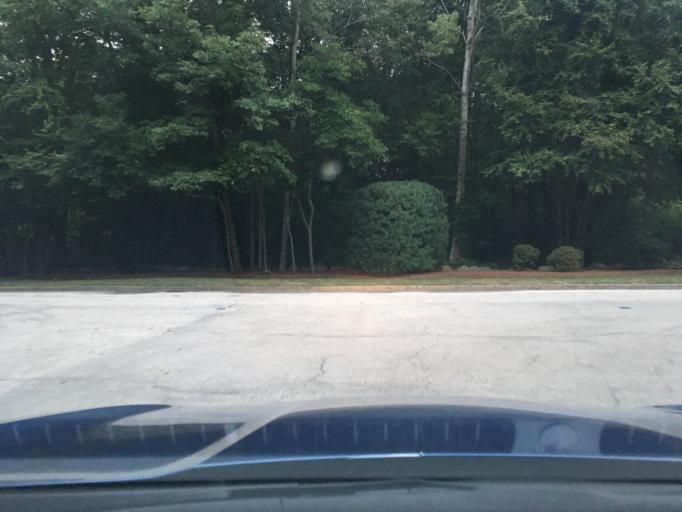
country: US
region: Rhode Island
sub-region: Kent County
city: West Warwick
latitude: 41.6544
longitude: -71.5158
